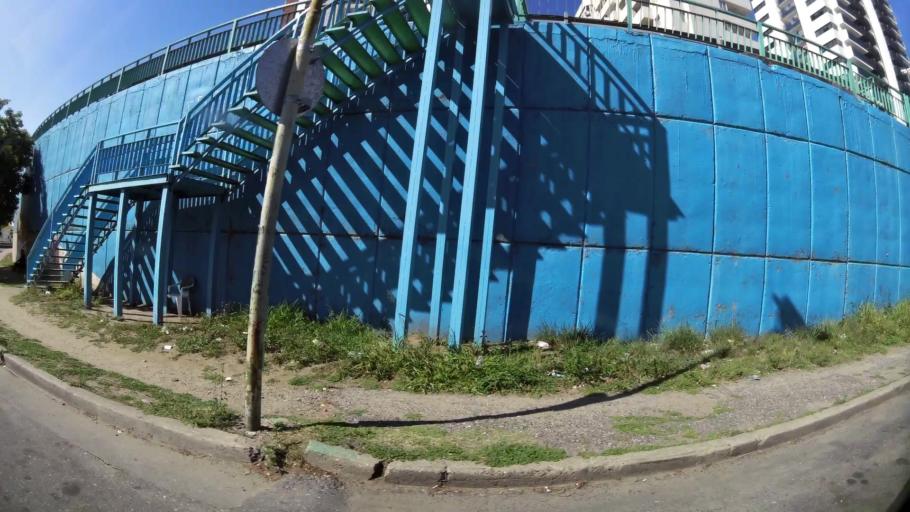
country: AR
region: Cordoba
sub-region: Departamento de Capital
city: Cordoba
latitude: -31.4234
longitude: -64.1758
